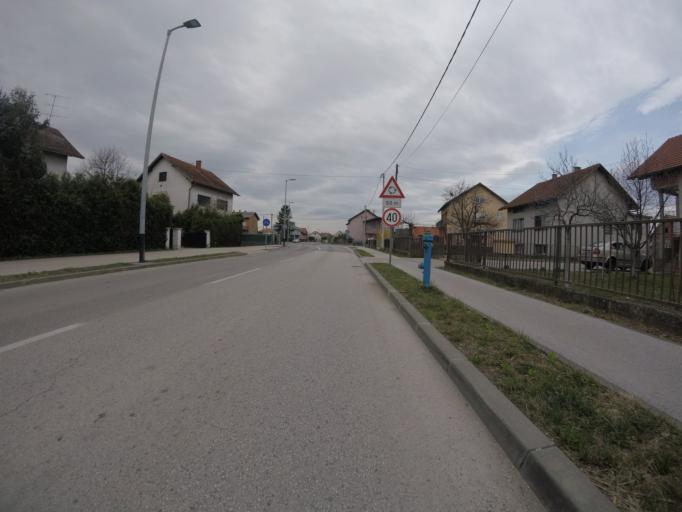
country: HR
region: Zagrebacka
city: Gradici
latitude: 45.7079
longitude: 16.0420
